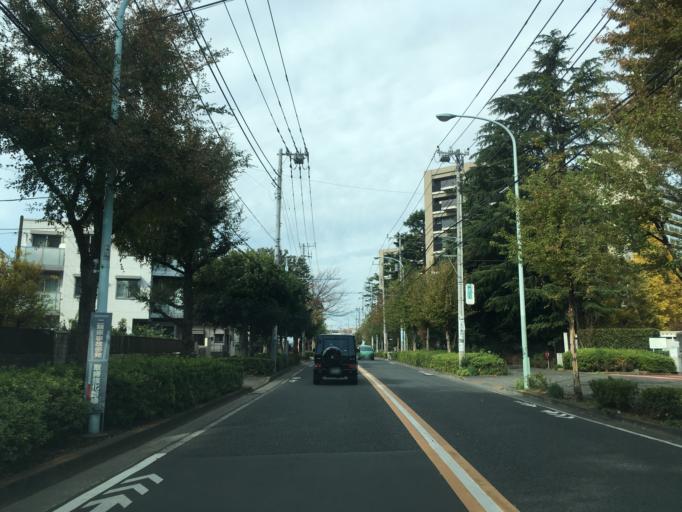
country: JP
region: Tokyo
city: Chofugaoka
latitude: 35.6354
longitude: 139.5771
